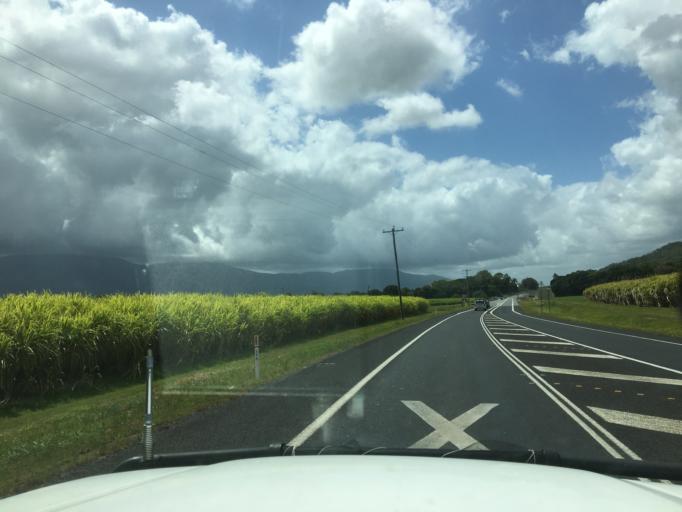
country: AU
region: Queensland
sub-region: Cairns
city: Woree
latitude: -17.1020
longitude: 145.7932
